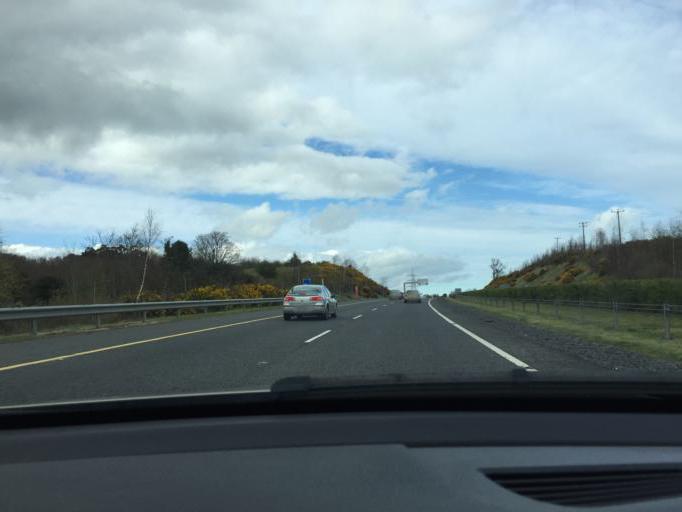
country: IE
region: Leinster
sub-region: Wicklow
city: Ashford
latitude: 53.0343
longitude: -6.0907
